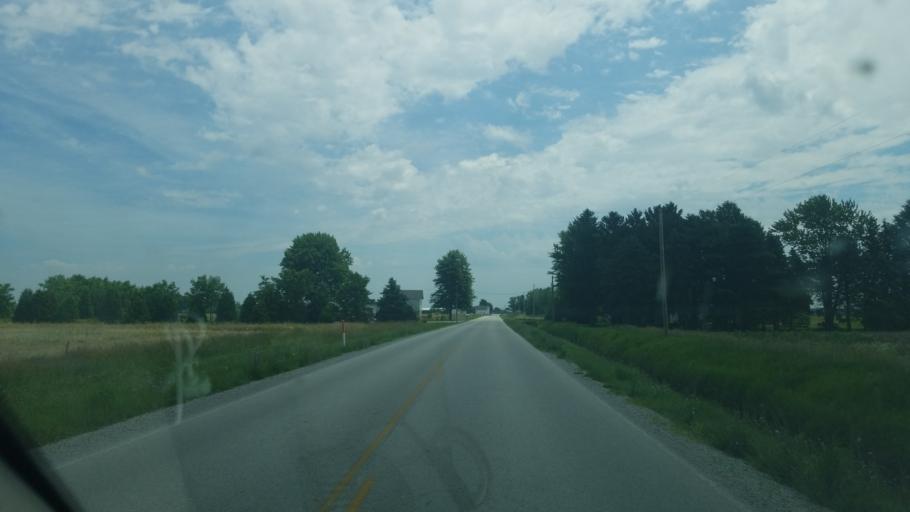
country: US
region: Ohio
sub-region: Wood County
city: Bowling Green
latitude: 41.2968
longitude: -83.6016
